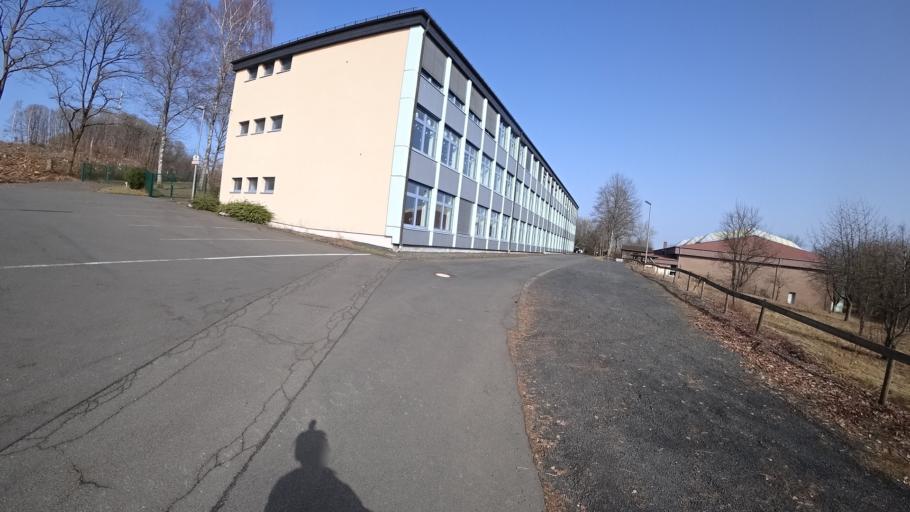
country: DE
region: Rheinland-Pfalz
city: Gebhardshain
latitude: 50.7403
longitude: 7.8243
